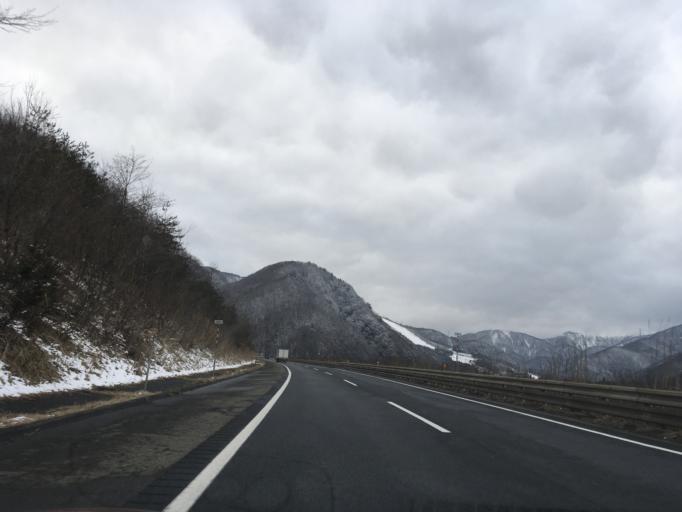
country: JP
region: Yamagata
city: Yamagata-shi
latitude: 38.2124
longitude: 140.5378
